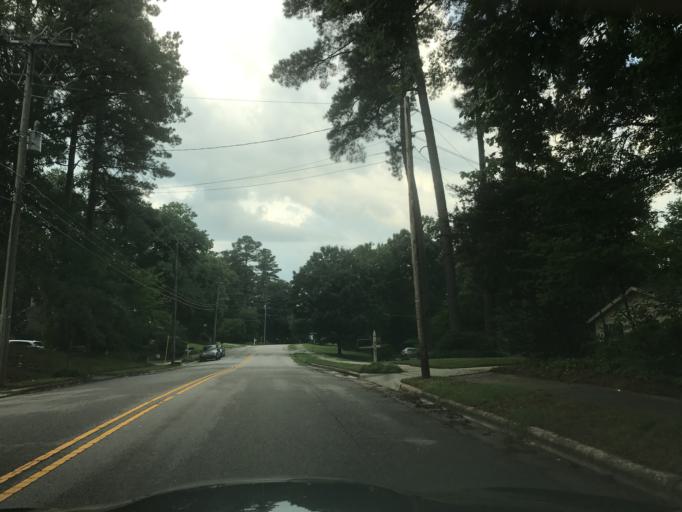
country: US
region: North Carolina
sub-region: Wake County
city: West Raleigh
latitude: 35.8433
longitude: -78.6516
